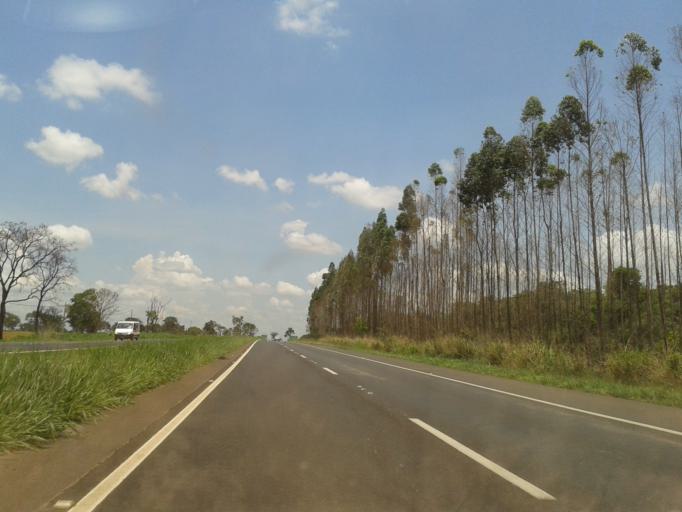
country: BR
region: Minas Gerais
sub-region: Monte Alegre De Minas
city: Monte Alegre de Minas
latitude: -18.8818
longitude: -48.6077
